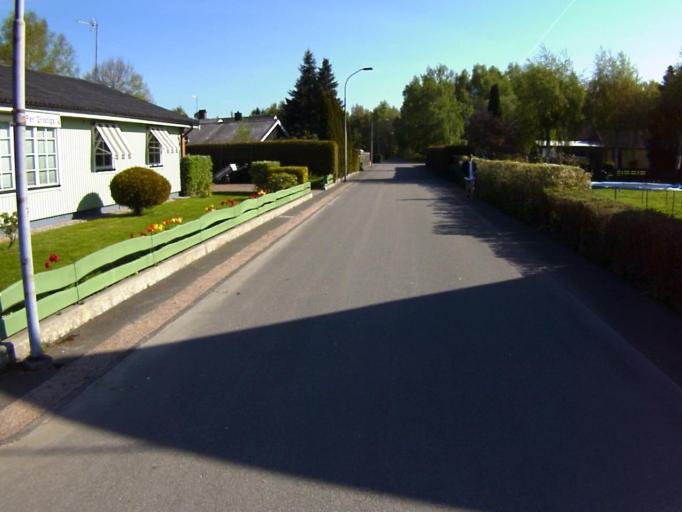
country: SE
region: Skane
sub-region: Kristianstads Kommun
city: Onnestad
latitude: 55.9331
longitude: 13.9643
